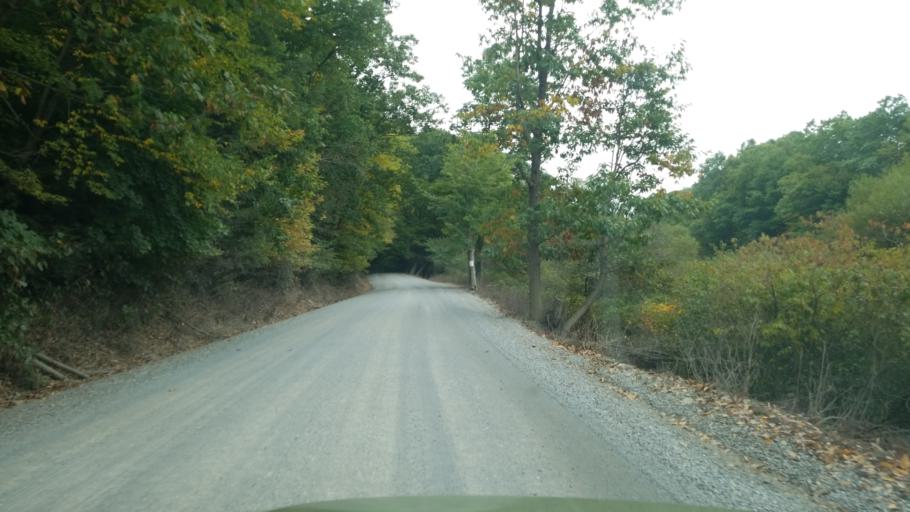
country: US
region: Pennsylvania
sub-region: Clearfield County
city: Curwensville
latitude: 40.9694
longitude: -78.4883
